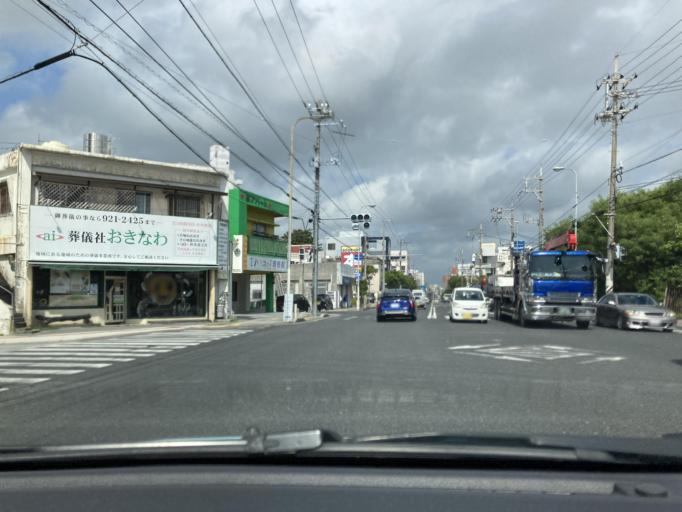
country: JP
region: Okinawa
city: Okinawa
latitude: 26.3350
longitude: 127.8179
